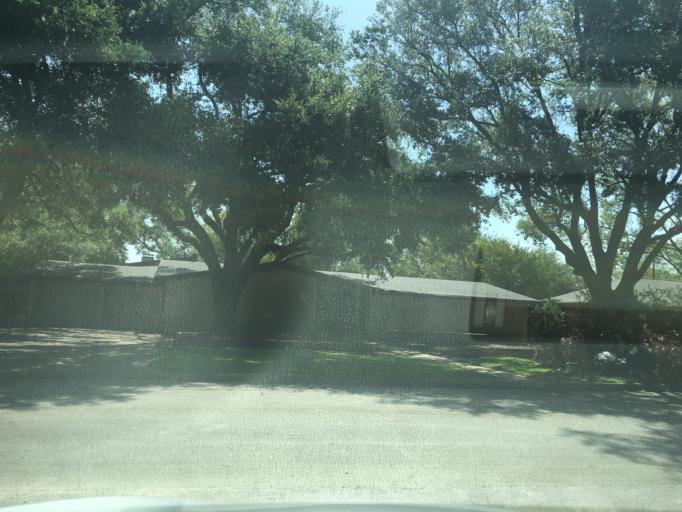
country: US
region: Texas
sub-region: Dallas County
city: University Park
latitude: 32.9016
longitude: -96.7740
